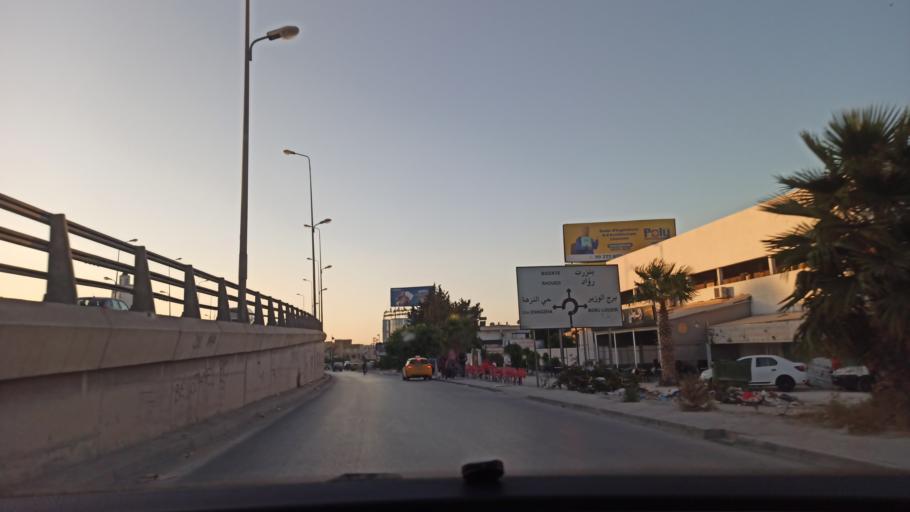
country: TN
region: Ariana
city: Ariana
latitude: 36.8633
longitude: 10.2015
